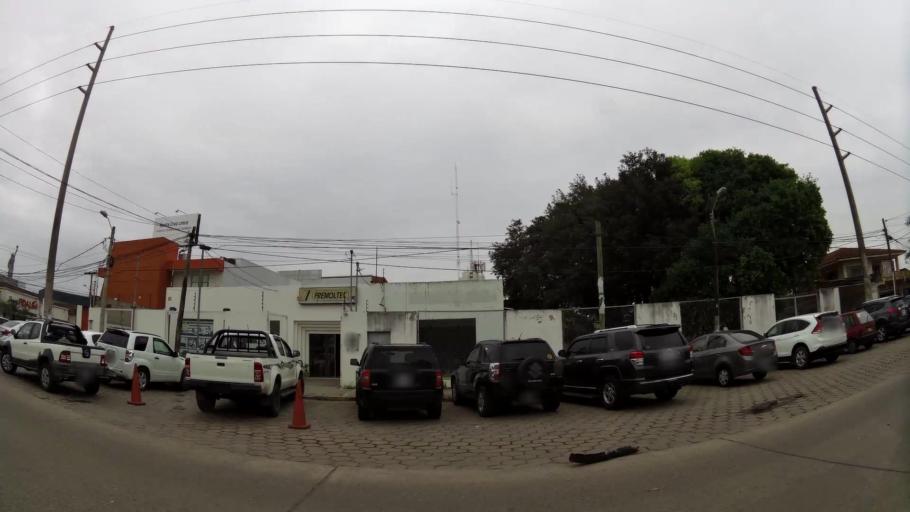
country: BO
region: Santa Cruz
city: Santa Cruz de la Sierra
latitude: -17.7578
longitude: -63.1791
